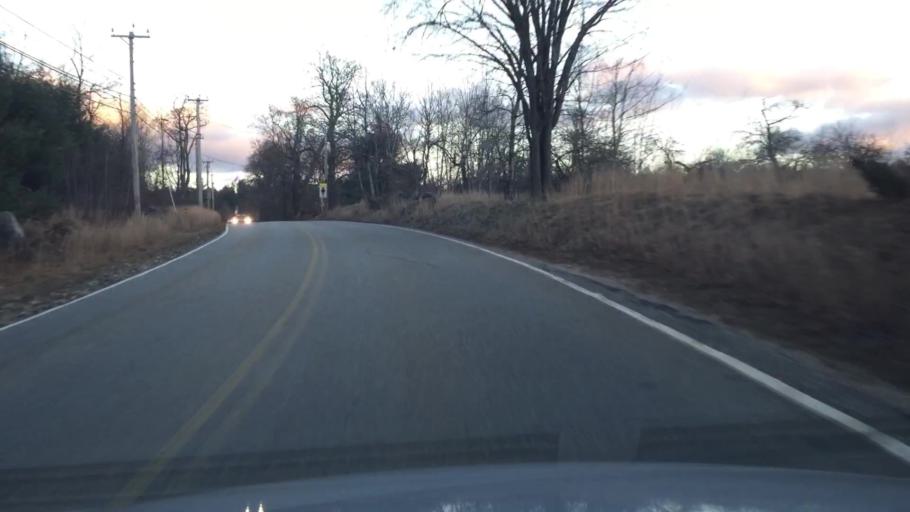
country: US
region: Massachusetts
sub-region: Worcester County
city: Princeton
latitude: 42.4438
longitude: -71.8467
